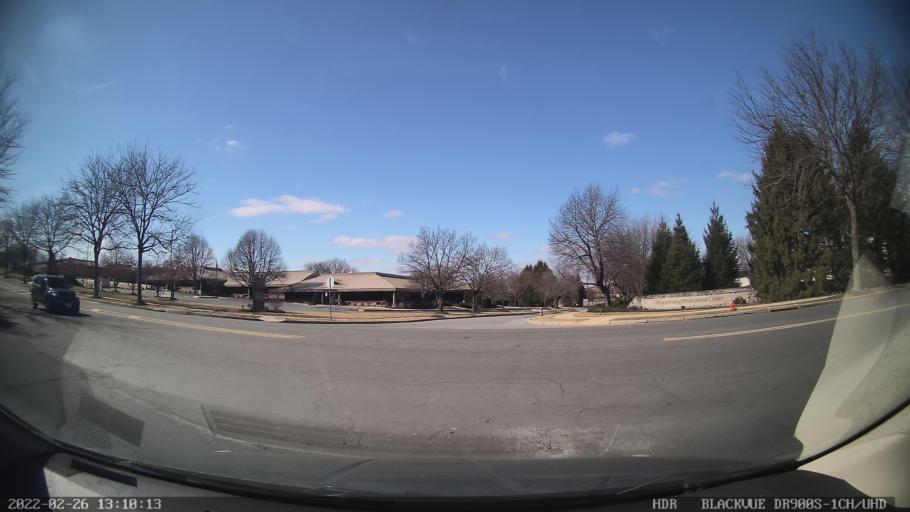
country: US
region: Pennsylvania
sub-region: Berks County
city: Wyomissing Hills
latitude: 40.3498
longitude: -75.9686
